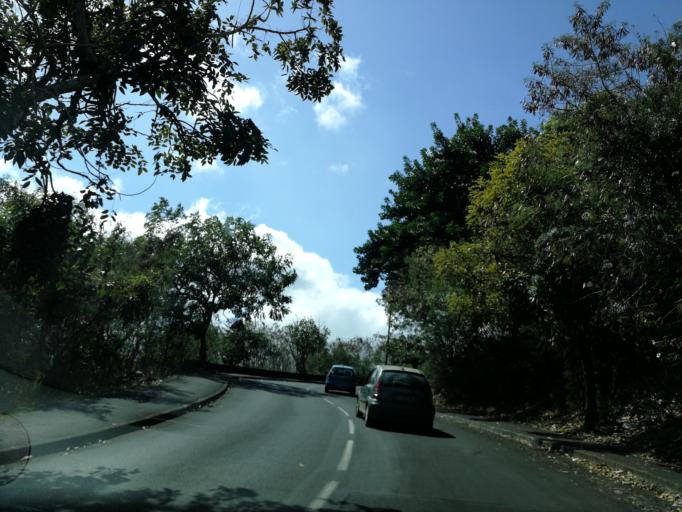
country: RE
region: Reunion
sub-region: Reunion
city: Saint-Denis
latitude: -20.9075
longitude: 55.4826
